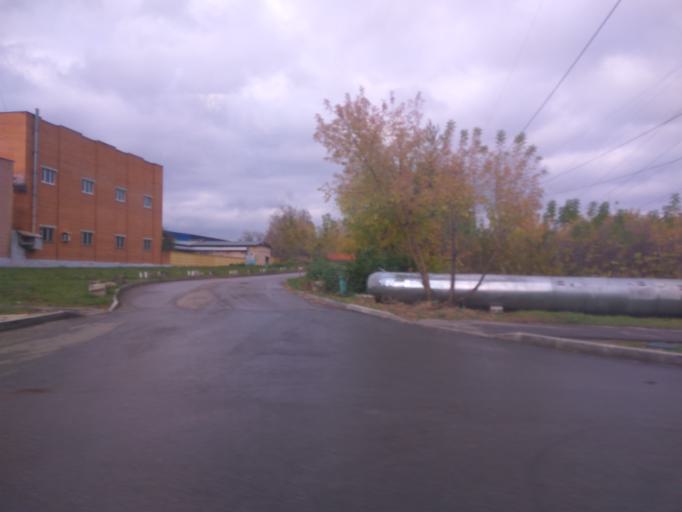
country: RU
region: Moscow
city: Tsaritsyno
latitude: 55.6285
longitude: 37.6453
